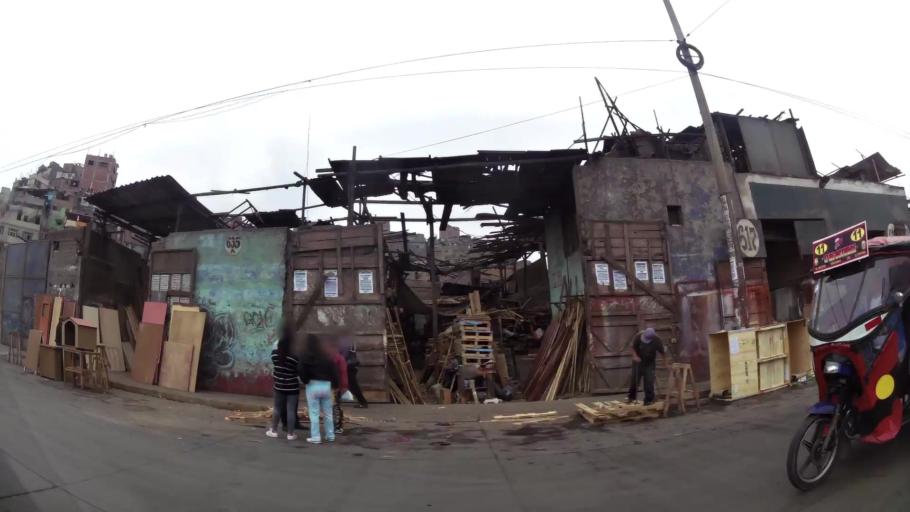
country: PE
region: Lima
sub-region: Lima
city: San Luis
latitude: -12.0607
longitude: -77.0054
